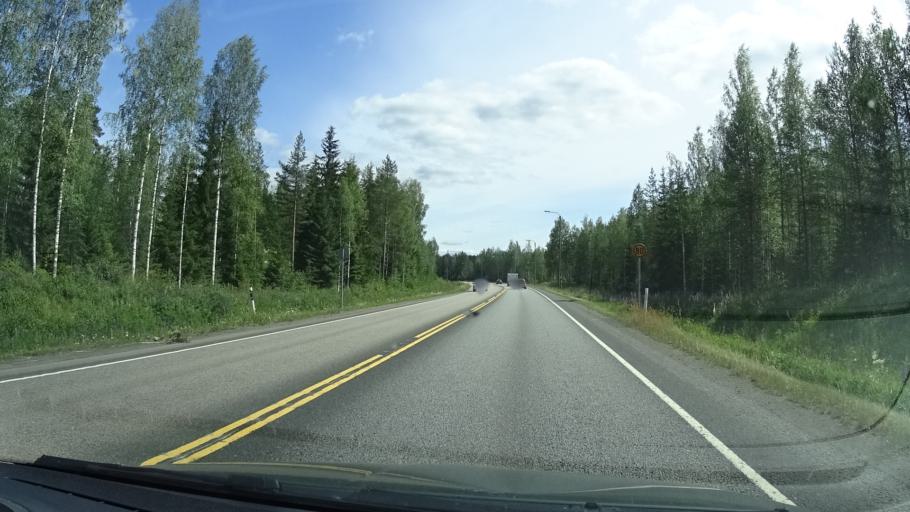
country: FI
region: Central Finland
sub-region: Jyvaeskylae
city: Muurame
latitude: 62.2674
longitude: 25.5191
